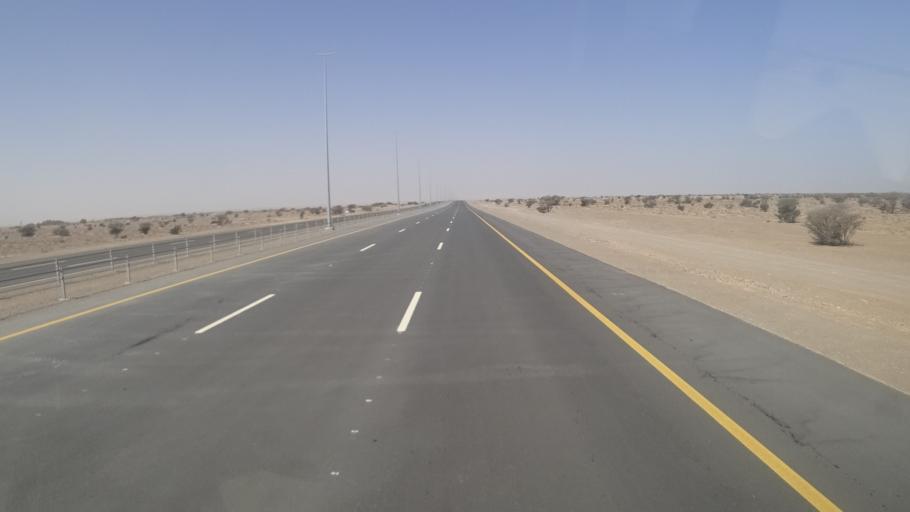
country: OM
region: Ash Sharqiyah
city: Sur
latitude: 22.2752
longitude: 59.2055
